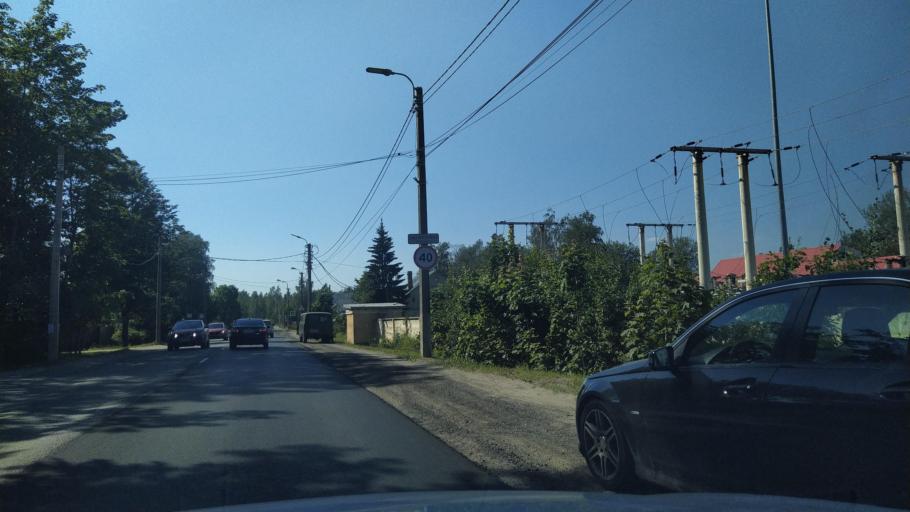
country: RU
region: St.-Petersburg
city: Beloostrov
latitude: 60.1458
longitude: 29.9988
